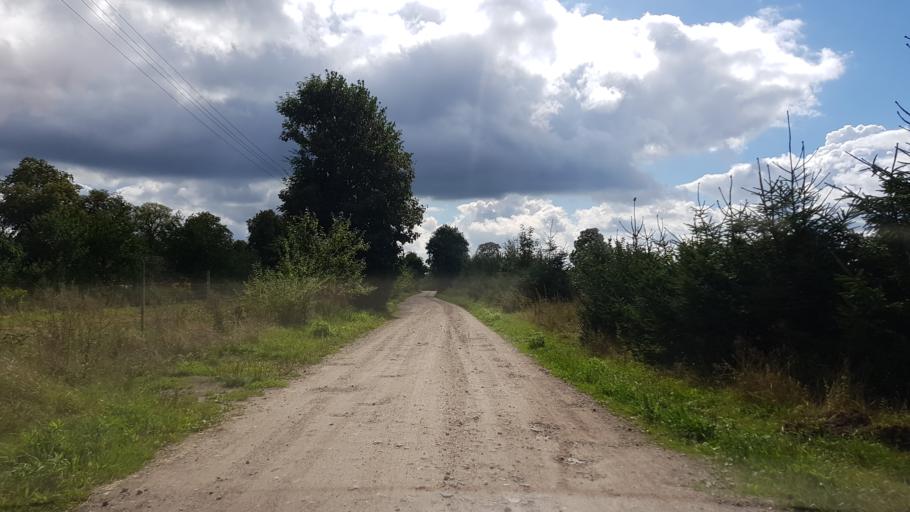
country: PL
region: West Pomeranian Voivodeship
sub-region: Powiat bialogardzki
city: Tychowo
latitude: 53.9954
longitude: 16.3055
